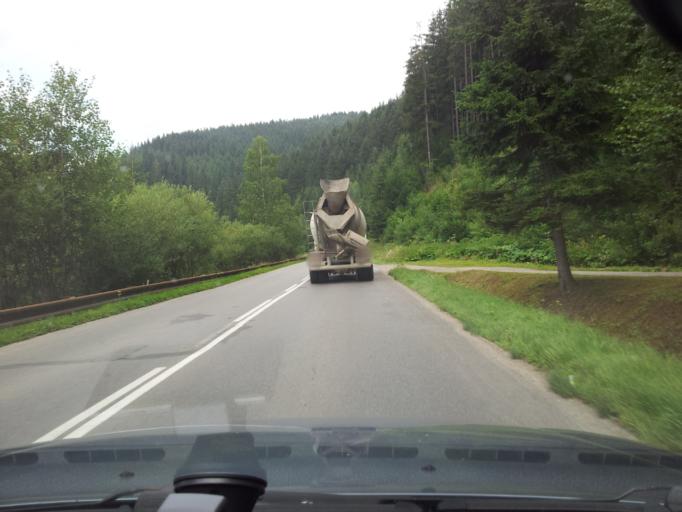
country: SK
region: Zilinsky
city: Namestovo
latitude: 49.3819
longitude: 19.3891
